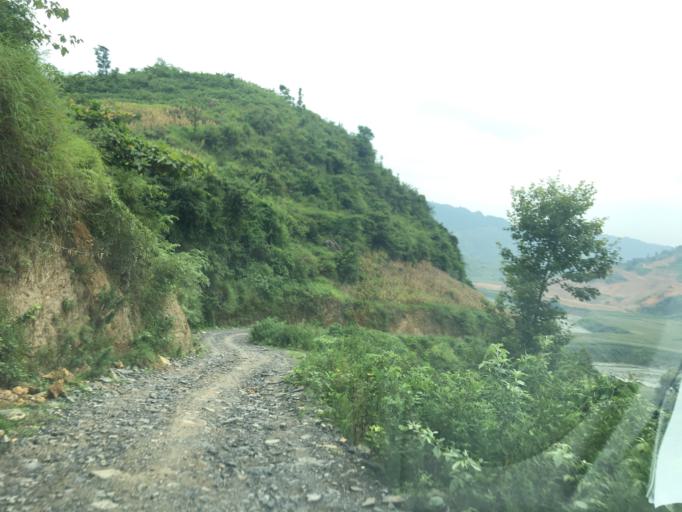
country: CN
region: Guangxi Zhuangzu Zizhiqu
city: Xinzhou
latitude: 25.1767
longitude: 105.7310
